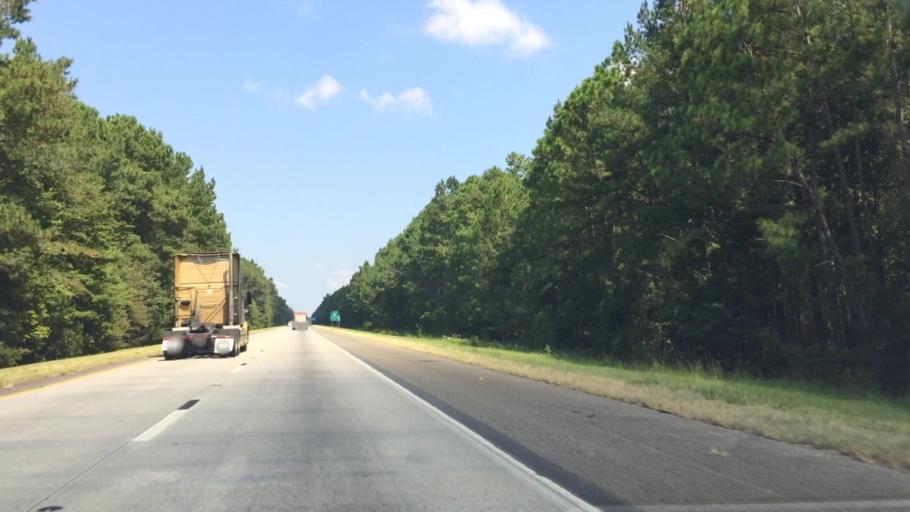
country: US
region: South Carolina
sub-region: Dorchester County
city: Saint George
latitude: 33.0645
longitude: -80.6614
